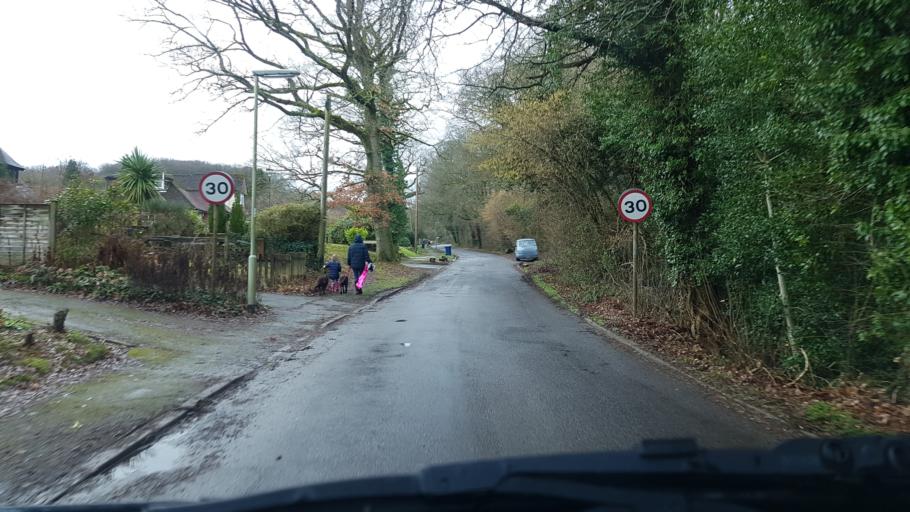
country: GB
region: England
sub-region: Surrey
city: Haslemere
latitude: 51.1041
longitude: -0.6833
